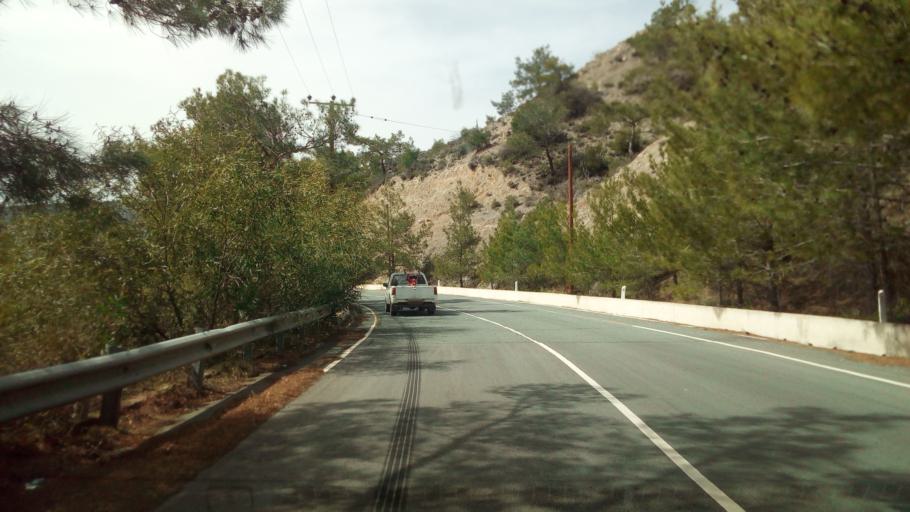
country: CY
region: Limassol
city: Pelendri
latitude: 34.8678
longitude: 32.9284
